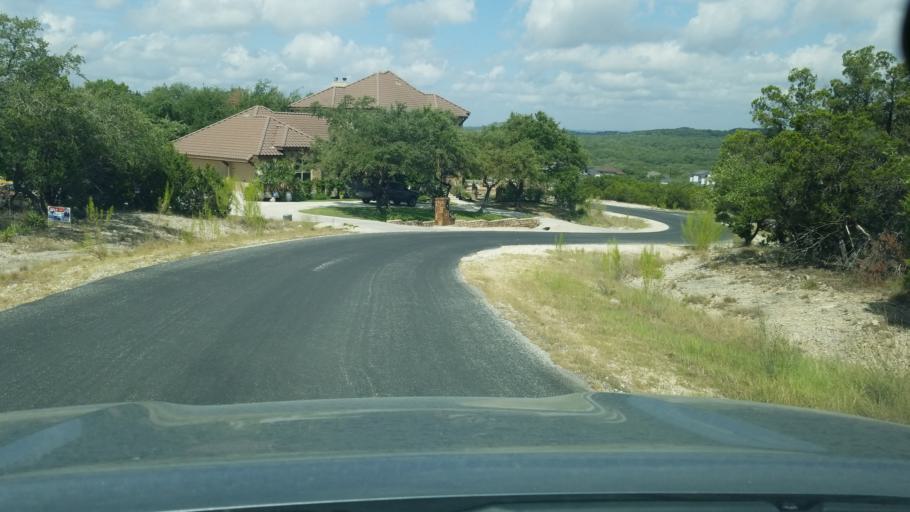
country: US
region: Texas
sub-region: Bexar County
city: Timberwood Park
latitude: 29.6856
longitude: -98.5178
